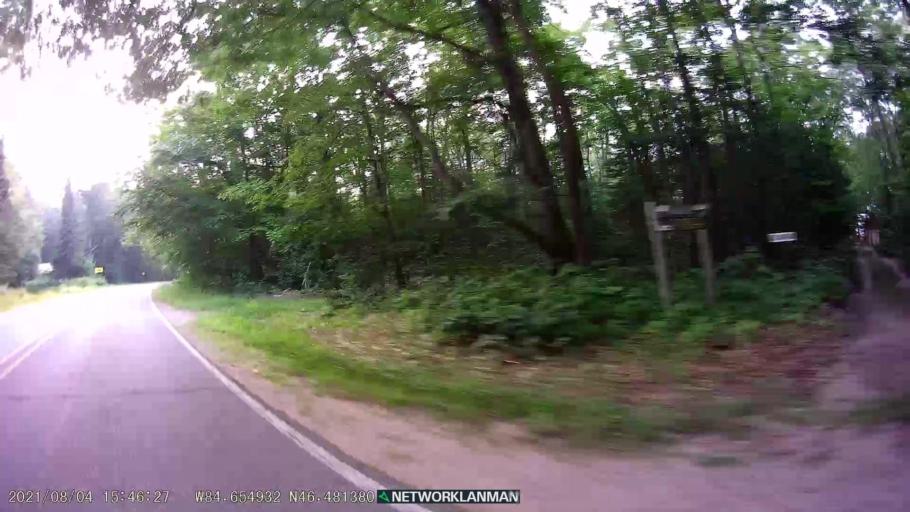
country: US
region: Michigan
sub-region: Chippewa County
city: Sault Ste. Marie
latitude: 46.4814
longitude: -84.6554
